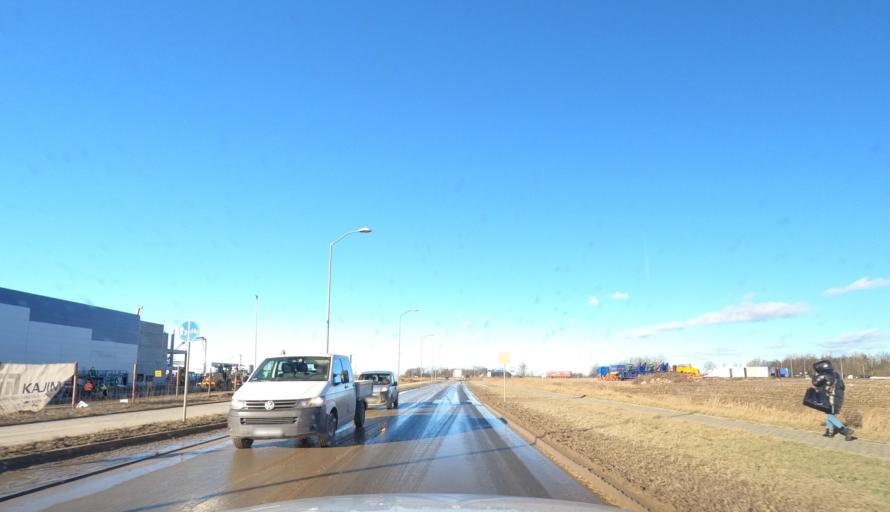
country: PL
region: West Pomeranian Voivodeship
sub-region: Powiat pyrzycki
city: Warnice
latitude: 53.2892
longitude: 14.9632
